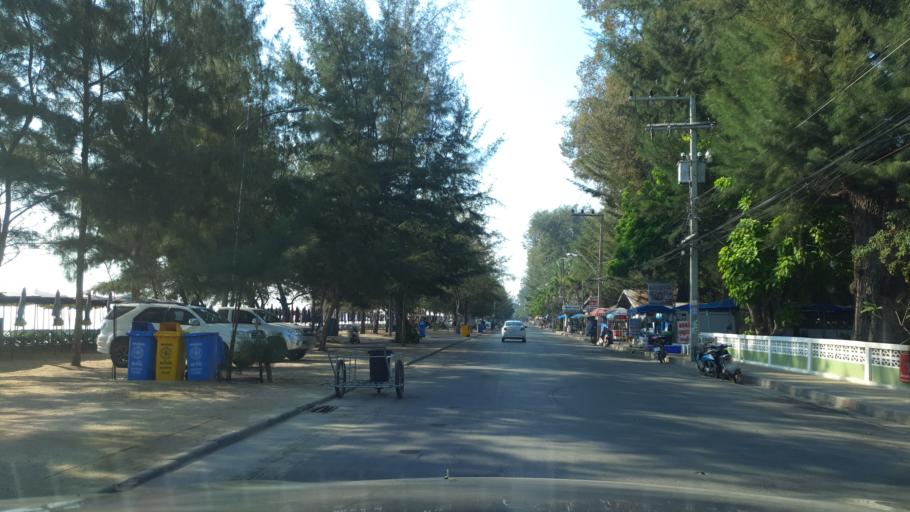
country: TH
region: Phetchaburi
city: Cha-am
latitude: 12.7889
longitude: 99.9817
